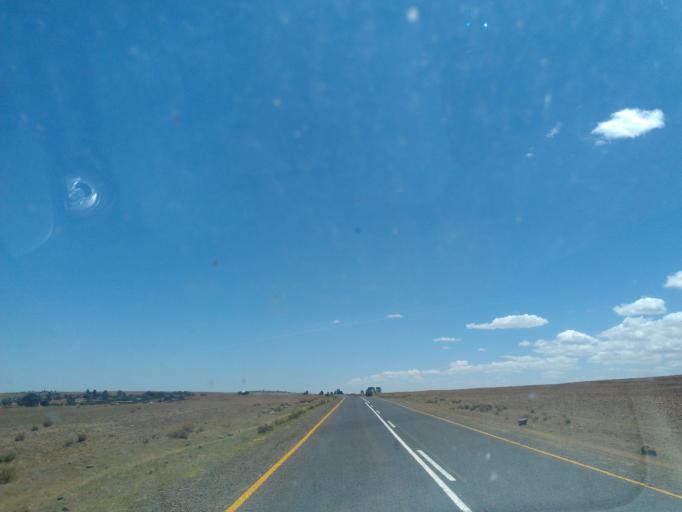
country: LS
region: Berea
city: Teyateyaneng
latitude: -29.2603
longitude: 27.7145
